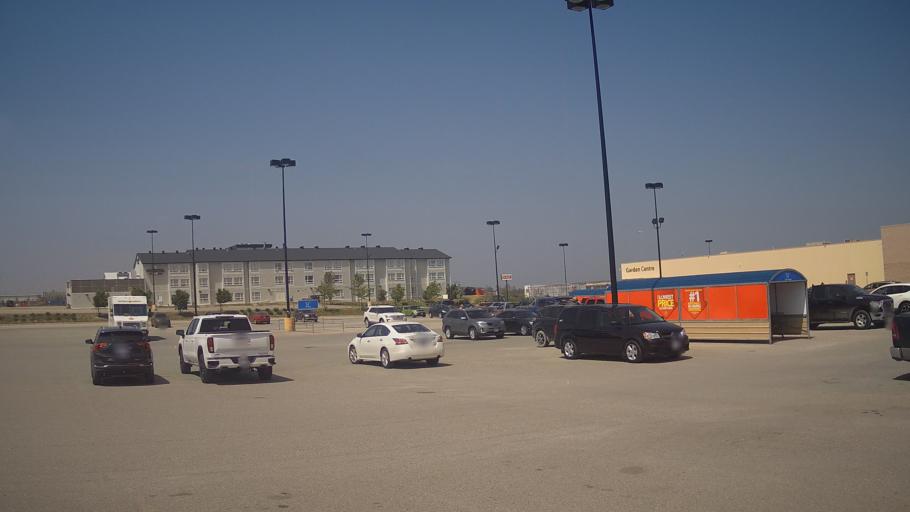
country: CA
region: Ontario
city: Timmins
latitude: 48.4737
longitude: -81.3932
